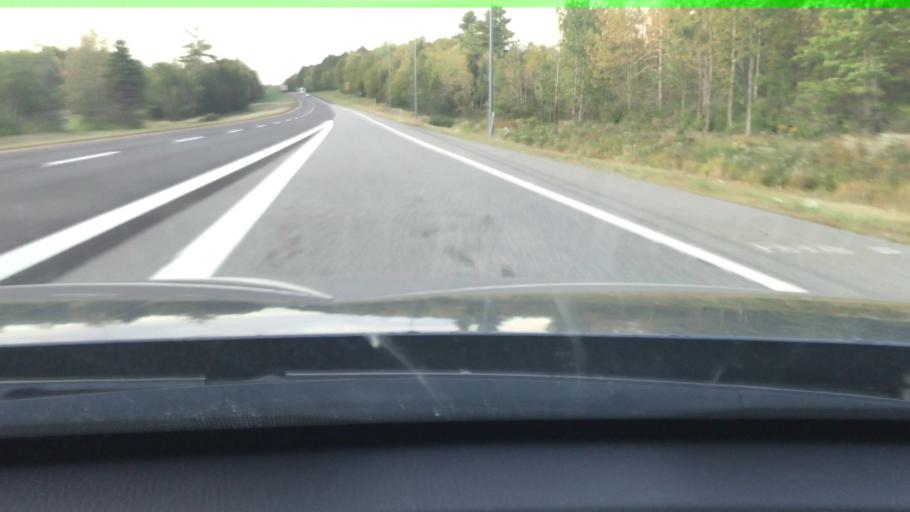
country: US
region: Maine
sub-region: Sagadahoc County
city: Richmond
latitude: 44.0953
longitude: -69.8734
